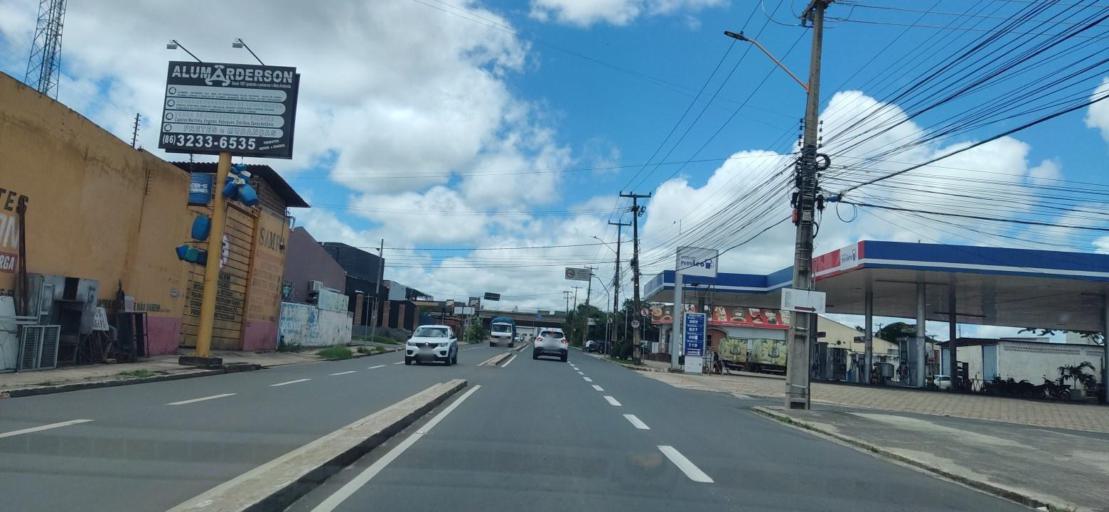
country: BR
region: Piaui
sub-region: Teresina
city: Teresina
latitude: -5.0889
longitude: -42.7624
